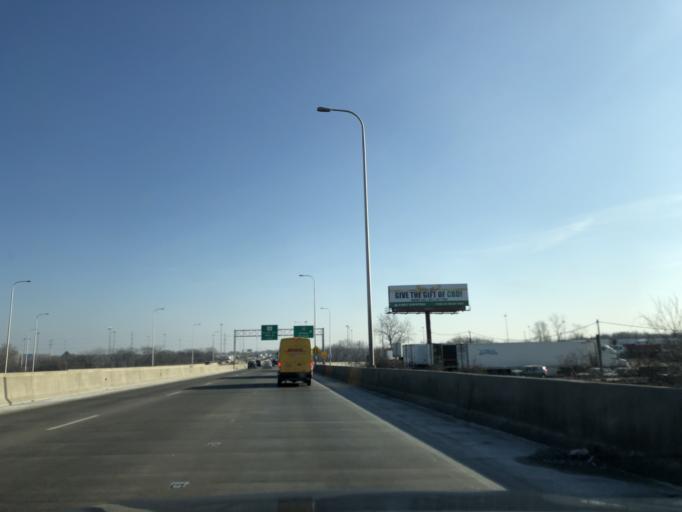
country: US
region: Illinois
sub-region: Cook County
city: Summit
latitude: 41.7959
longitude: -87.8278
